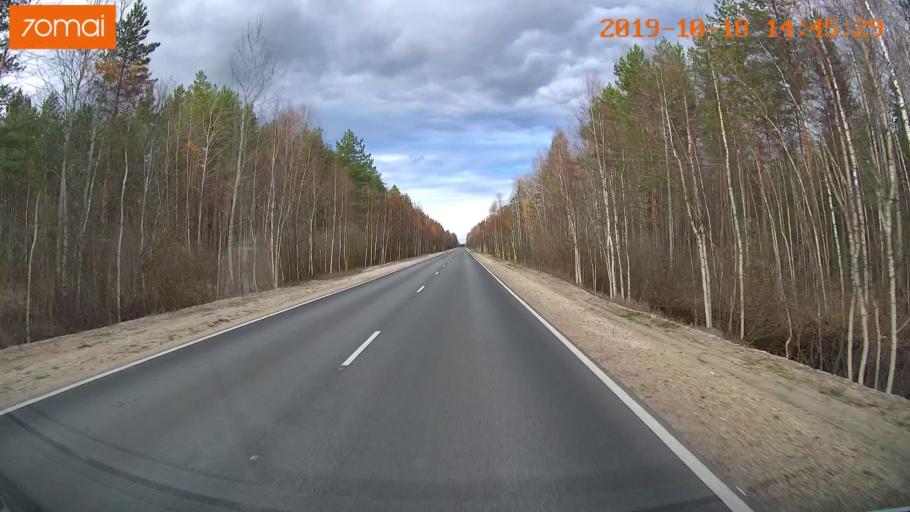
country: RU
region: Vladimir
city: Velikodvorskiy
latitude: 55.3557
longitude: 40.6790
